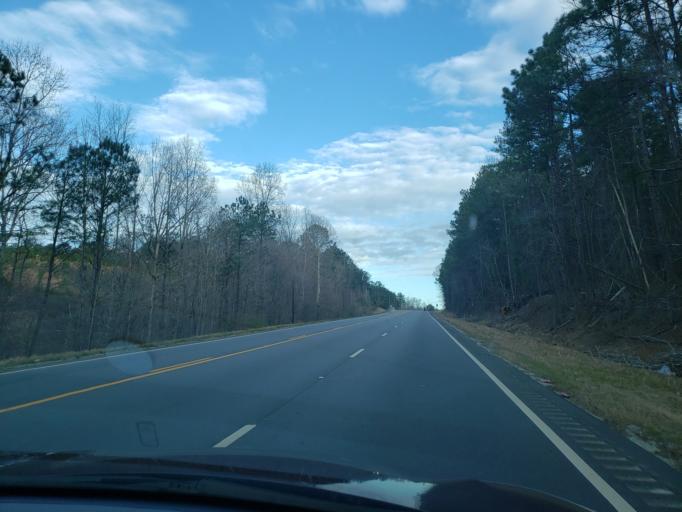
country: US
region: Alabama
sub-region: Randolph County
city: Wedowee
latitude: 33.2489
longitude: -85.4501
